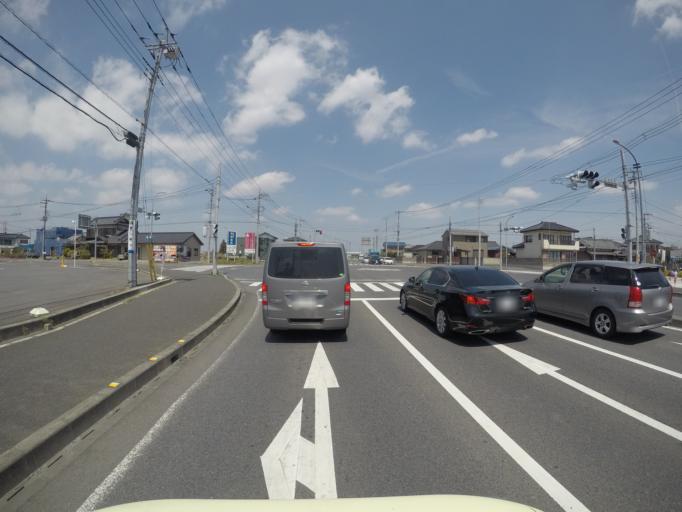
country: JP
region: Tochigi
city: Mibu
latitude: 36.4314
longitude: 139.7953
